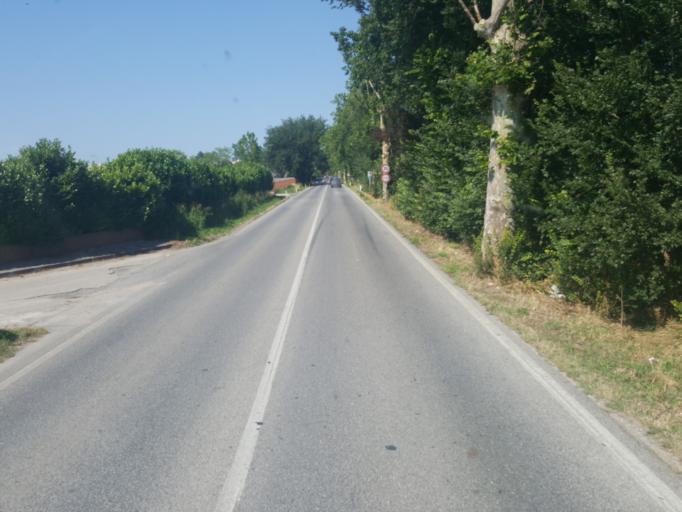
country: IT
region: The Marches
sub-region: Provincia di Ancona
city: Monsano
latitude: 43.5599
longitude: 13.2887
